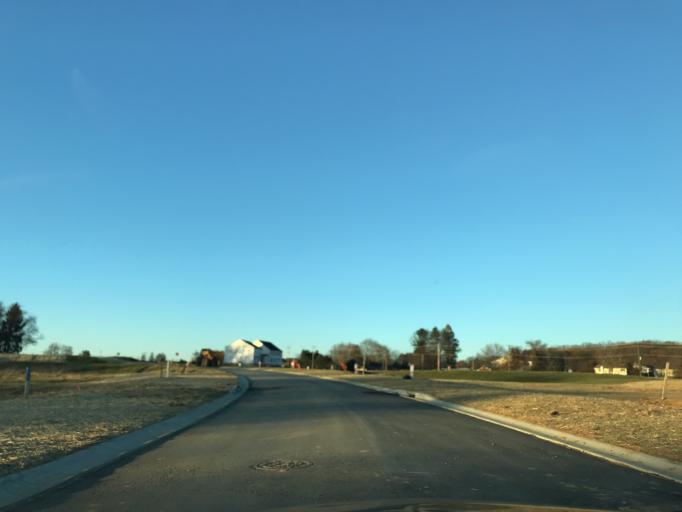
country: US
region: Maryland
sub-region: Howard County
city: Highland
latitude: 39.1993
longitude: -76.9410
